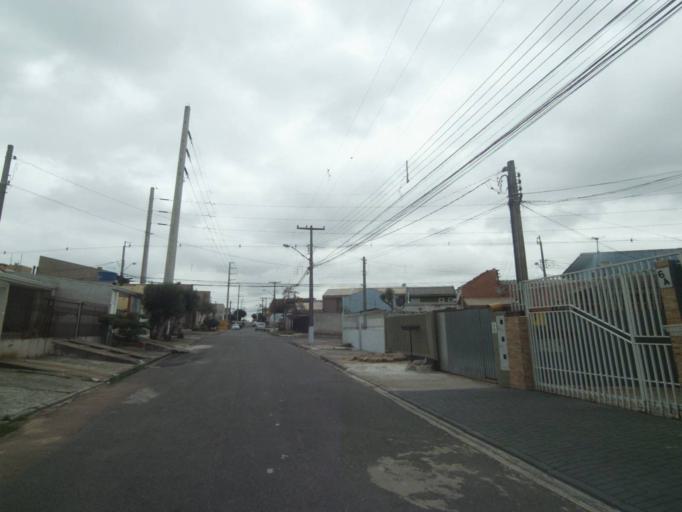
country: BR
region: Parana
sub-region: Sao Jose Dos Pinhais
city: Sao Jose dos Pinhais
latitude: -25.5432
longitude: -49.2701
